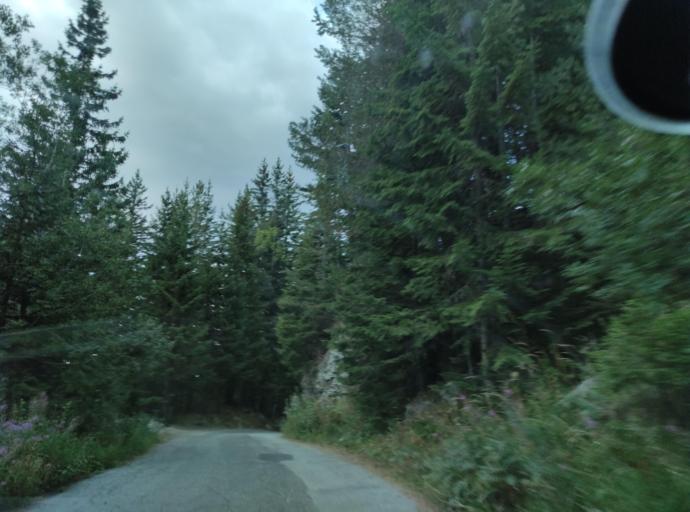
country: BG
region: Blagoevgrad
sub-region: Obshtina Bansko
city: Bansko
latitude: 41.7732
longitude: 23.4338
